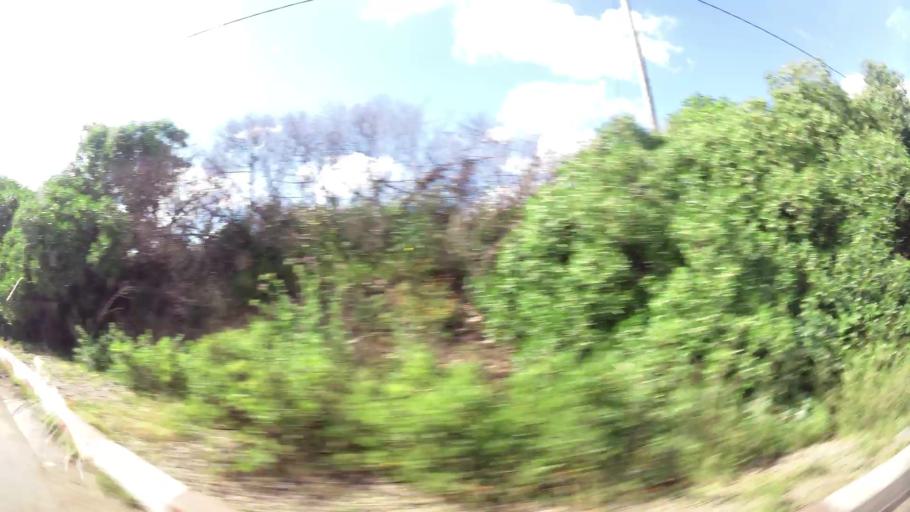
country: MA
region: Grand Casablanca
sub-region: Mediouna
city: Mediouna
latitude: 33.4095
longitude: -7.5391
